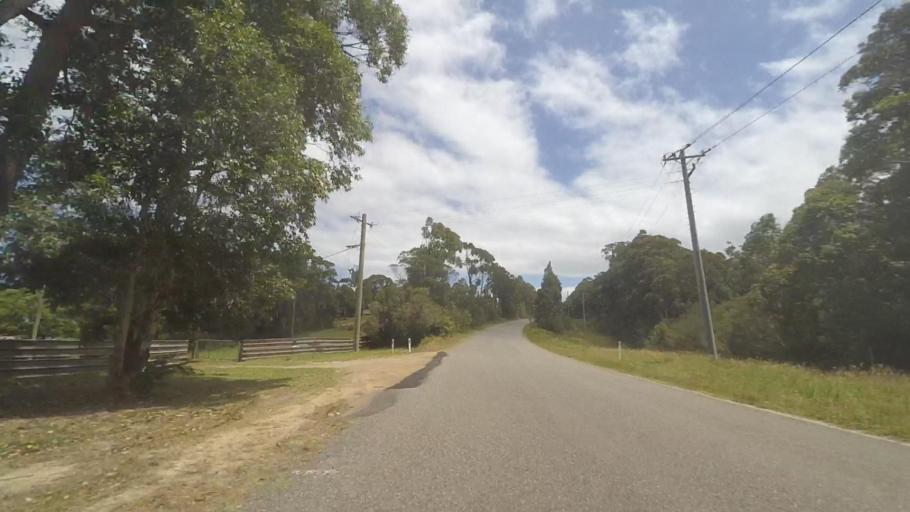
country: AU
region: New South Wales
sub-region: Shoalhaven Shire
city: Milton
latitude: -35.4096
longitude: 150.3558
